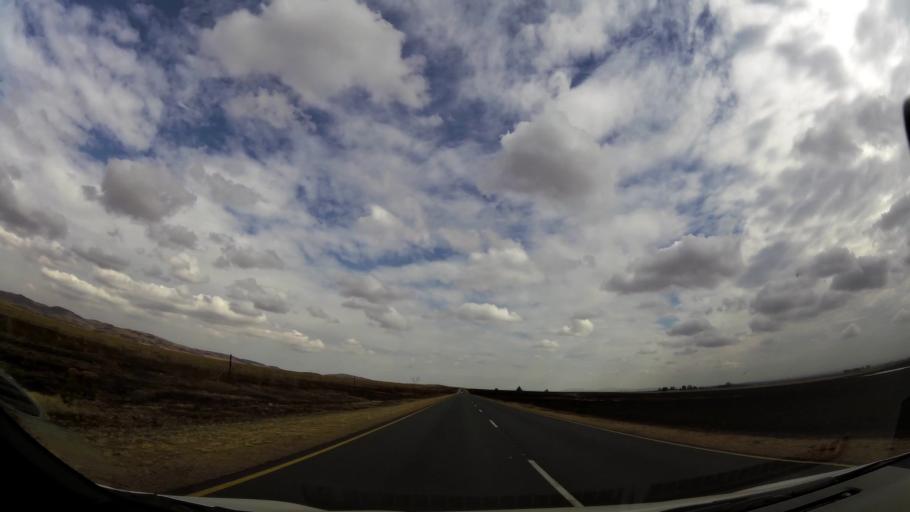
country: ZA
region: Gauteng
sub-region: Sedibeng District Municipality
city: Heidelberg
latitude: -26.4368
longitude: 28.2426
